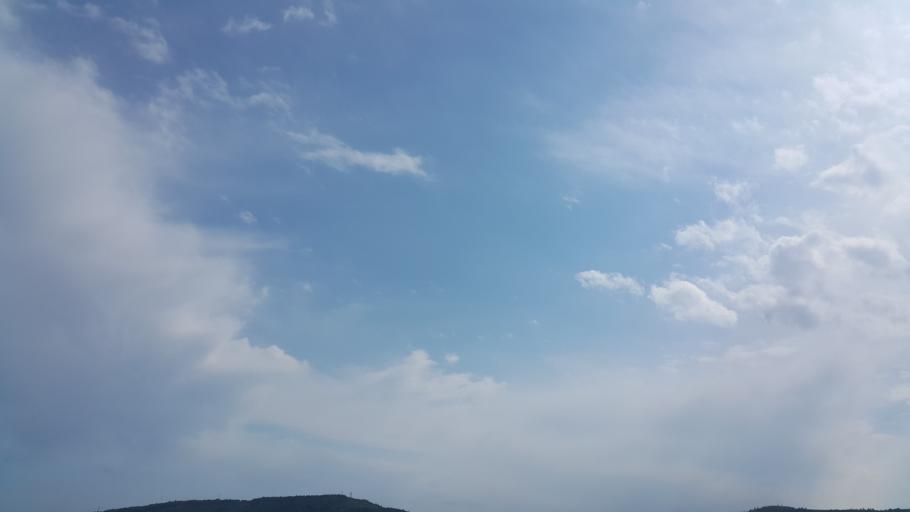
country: TR
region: Mersin
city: Tarsus
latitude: 36.9483
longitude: 34.7817
